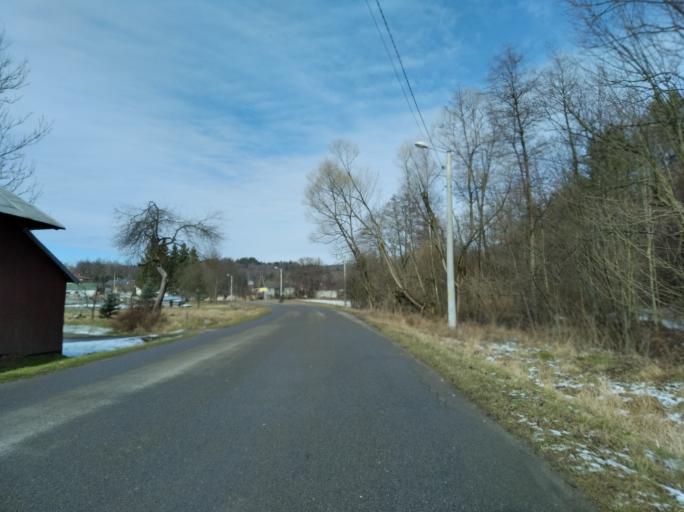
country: PL
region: Subcarpathian Voivodeship
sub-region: Powiat brzozowski
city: Jasienica Rosielna
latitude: 49.7518
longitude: 21.9144
